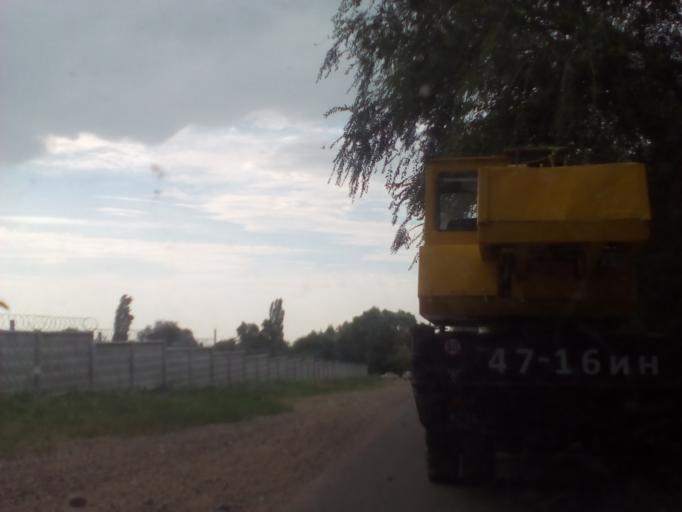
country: KZ
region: Almaty Oblysy
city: Burunday
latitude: 43.1603
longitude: 76.3822
